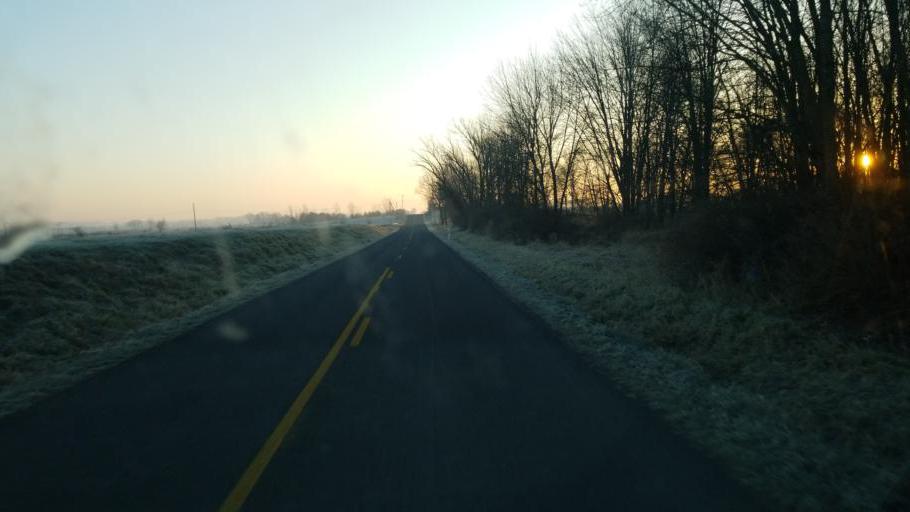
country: US
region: Ohio
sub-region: Medina County
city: Lodi
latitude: 41.0006
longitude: -82.0215
